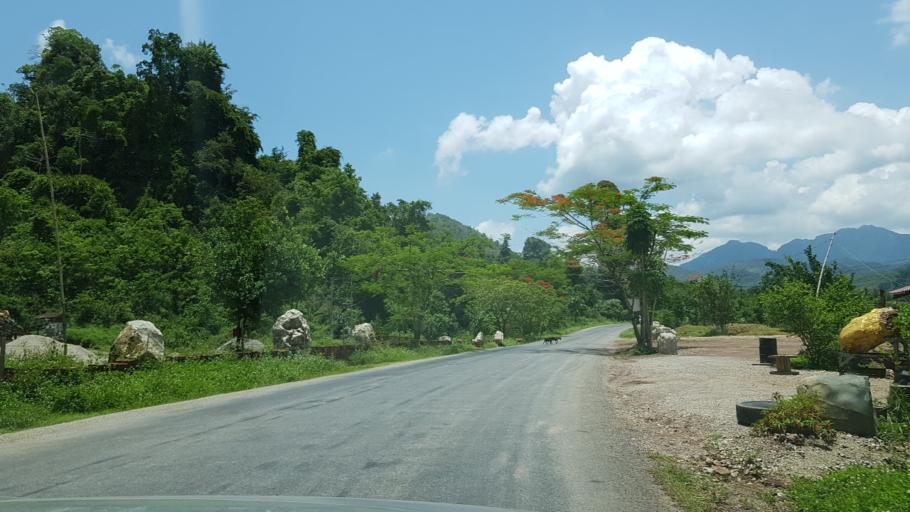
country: LA
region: Vientiane
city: Muang Kasi
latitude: 19.1265
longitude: 102.2611
